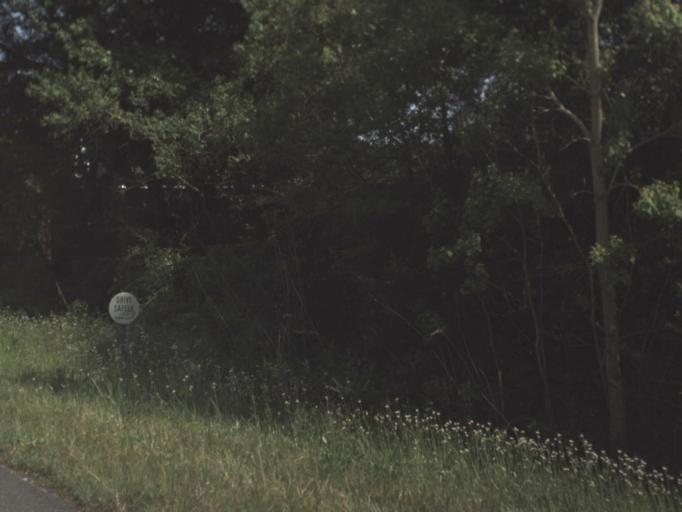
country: US
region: Florida
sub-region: Escambia County
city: Myrtle Grove
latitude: 30.4222
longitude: -87.3336
